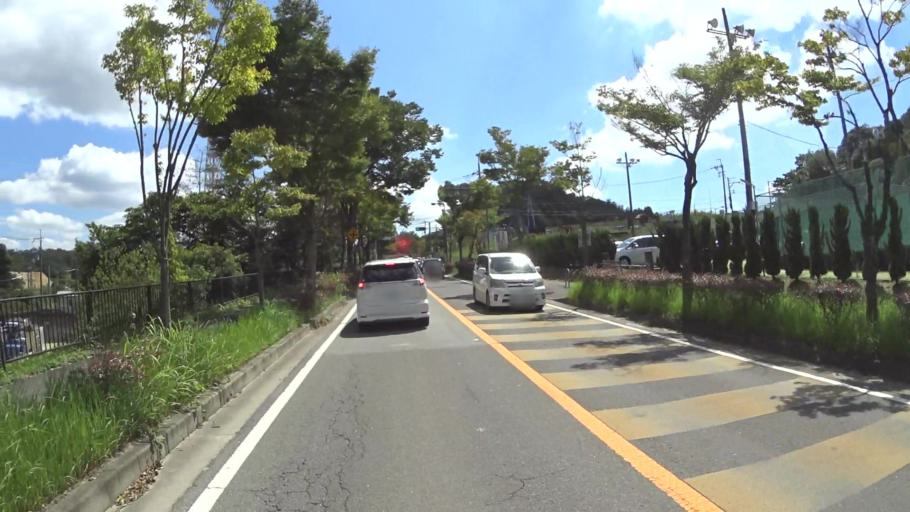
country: JP
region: Kyoto
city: Uji
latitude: 34.8612
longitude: 135.7988
